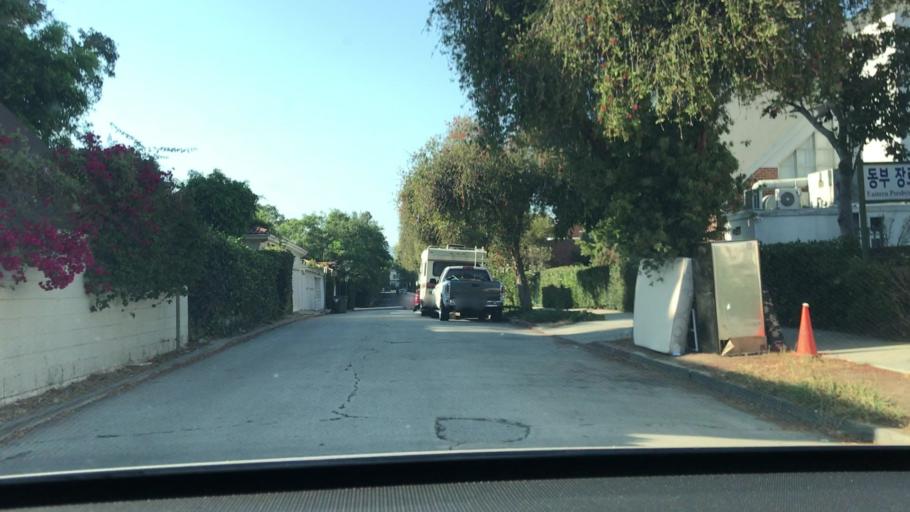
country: US
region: California
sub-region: Los Angeles County
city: Hollywood
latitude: 34.0626
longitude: -118.3178
